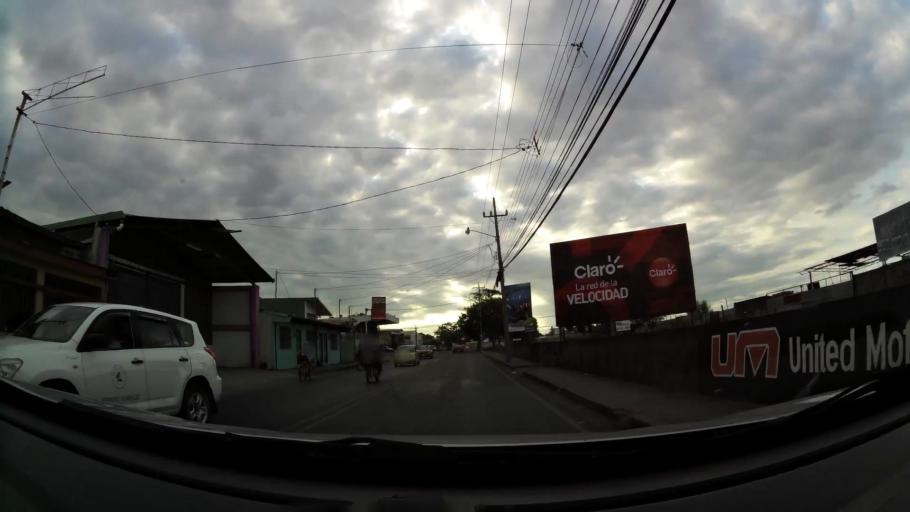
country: CR
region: Puntarenas
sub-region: Canton Central de Puntarenas
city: Puntarenas
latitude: 9.9785
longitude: -84.8242
